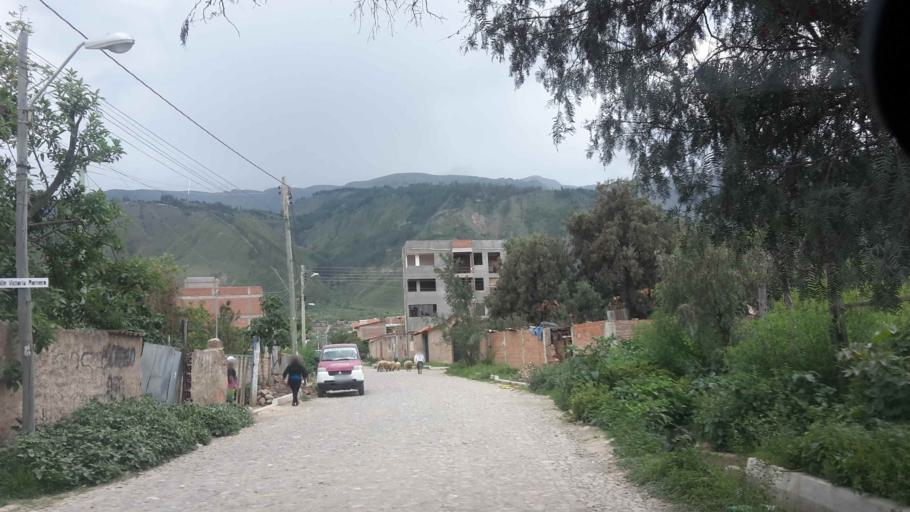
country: BO
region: Cochabamba
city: Cochabamba
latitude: -17.3330
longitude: -66.2225
